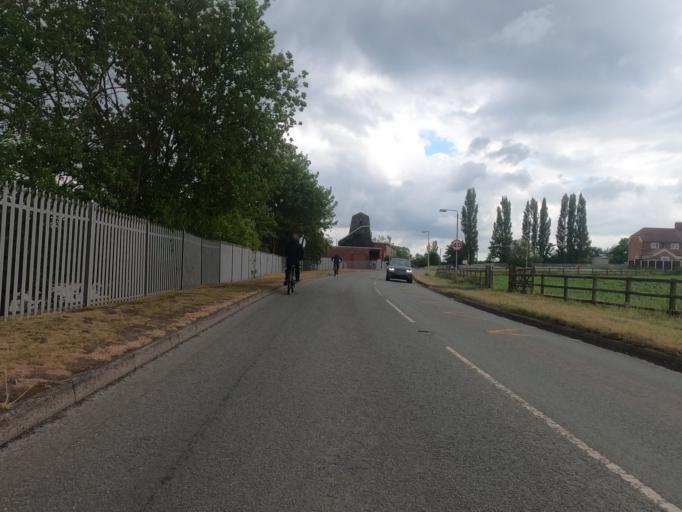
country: GB
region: England
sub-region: Cheshire West and Chester
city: Winsford
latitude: 53.2111
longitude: -2.5226
